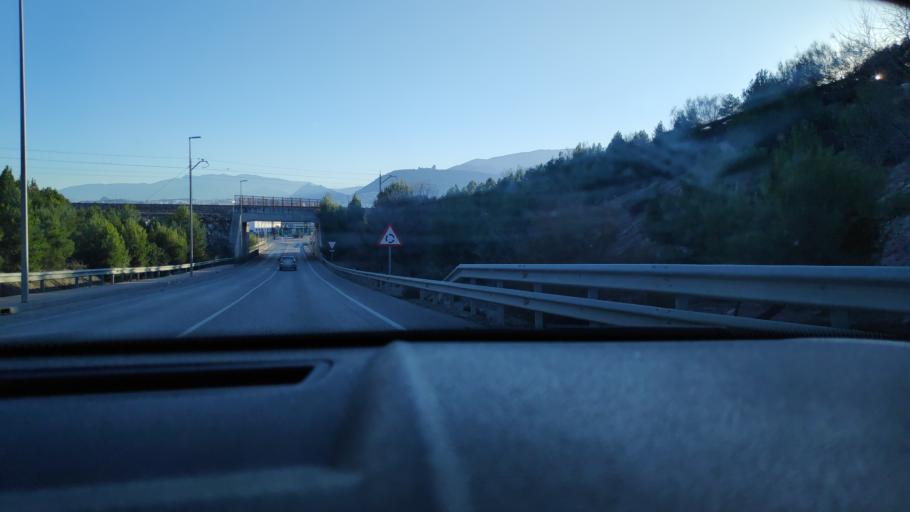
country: ES
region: Andalusia
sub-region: Provincia de Jaen
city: Jaen
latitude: 37.8047
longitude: -3.7881
